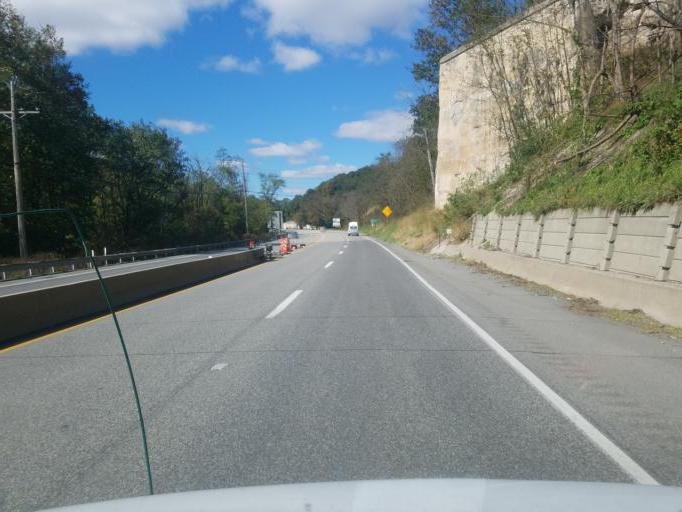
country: US
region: Pennsylvania
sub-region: Bedford County
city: Everett
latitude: 40.0107
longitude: -78.3875
